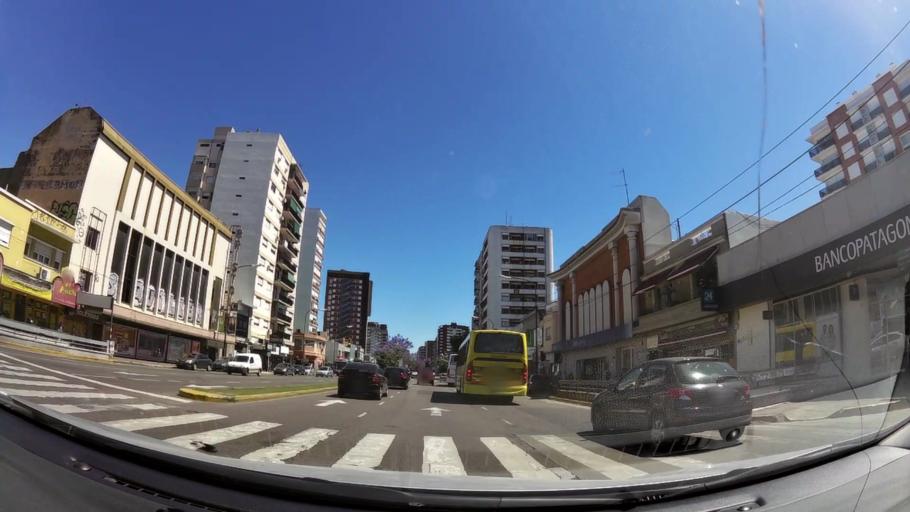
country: AR
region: Buenos Aires
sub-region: Partido de San Isidro
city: San Isidro
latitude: -34.4886
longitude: -58.5010
